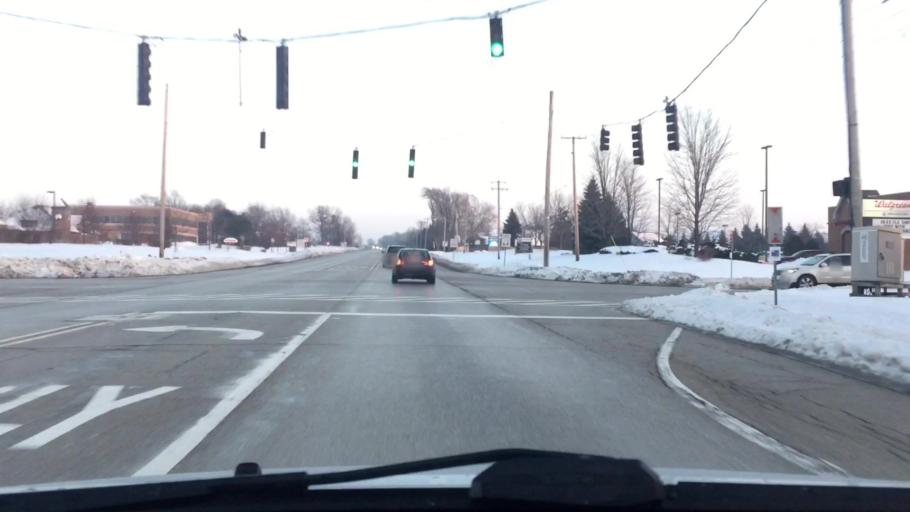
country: US
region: Illinois
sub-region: Kane County
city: Village of Campton Hills
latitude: 41.9186
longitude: -88.3591
